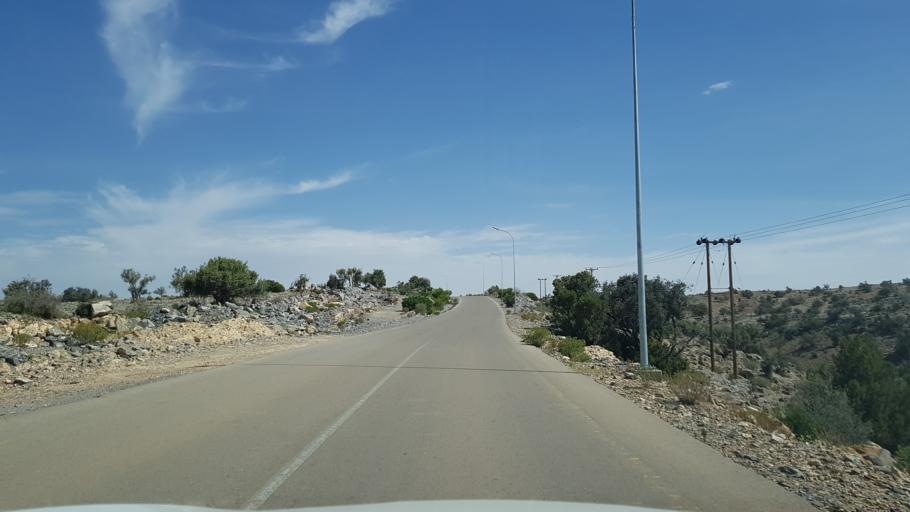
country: OM
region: Al Batinah
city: Bayt al `Awabi
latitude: 23.1274
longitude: 57.5989
